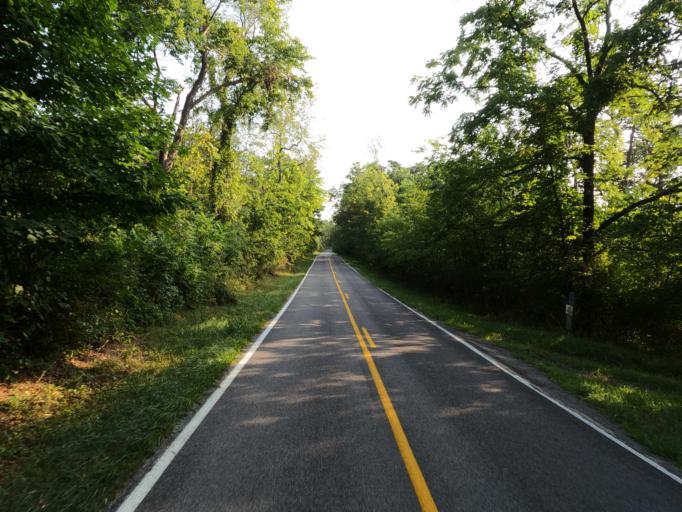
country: US
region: West Virginia
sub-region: Morgan County
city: Berkeley Springs
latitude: 39.6629
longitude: -78.2860
